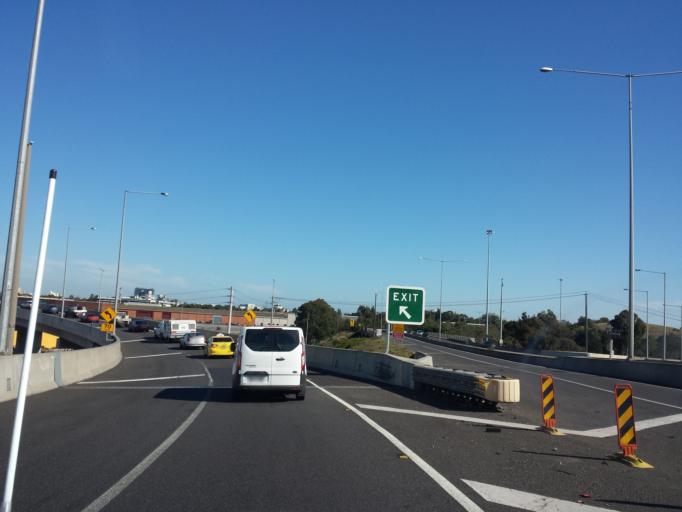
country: AU
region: Victoria
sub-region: Port Phillip
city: Port Melbourne
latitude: -37.8251
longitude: 144.9309
